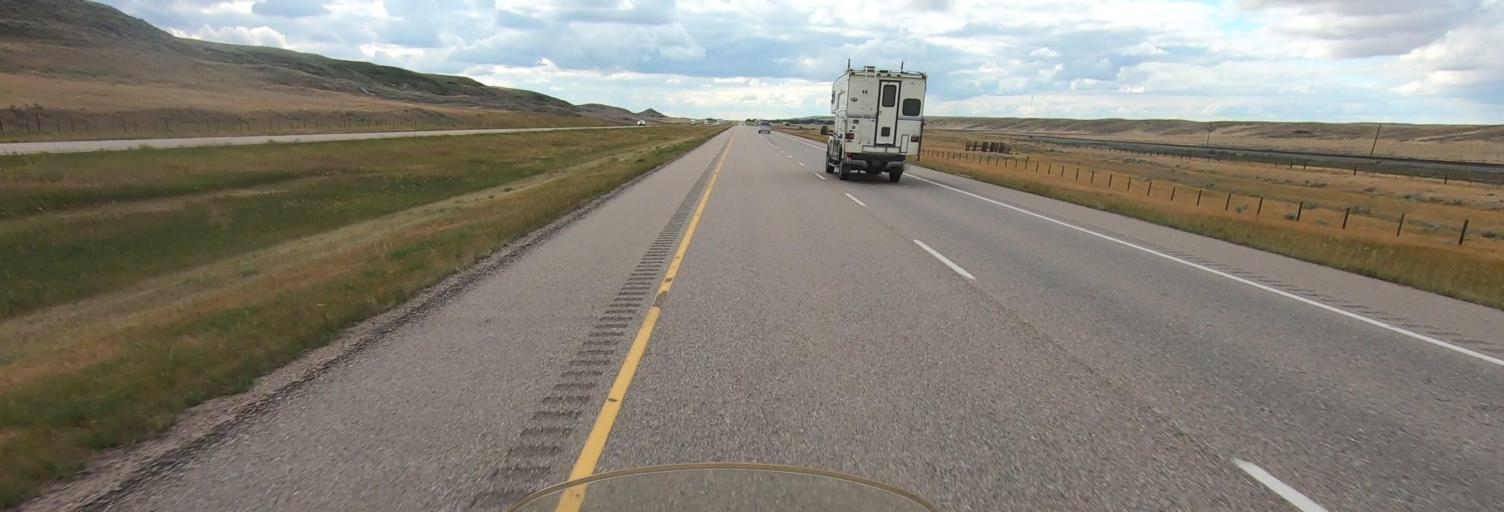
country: CA
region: Alberta
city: Medicine Hat
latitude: 49.9509
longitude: -110.2337
